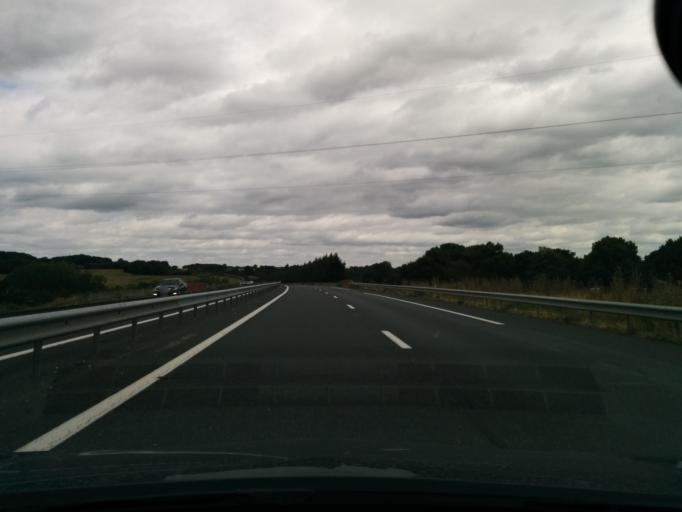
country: FR
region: Centre
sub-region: Departement de l'Indre
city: Le Pechereau
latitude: 46.5198
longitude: 1.5139
